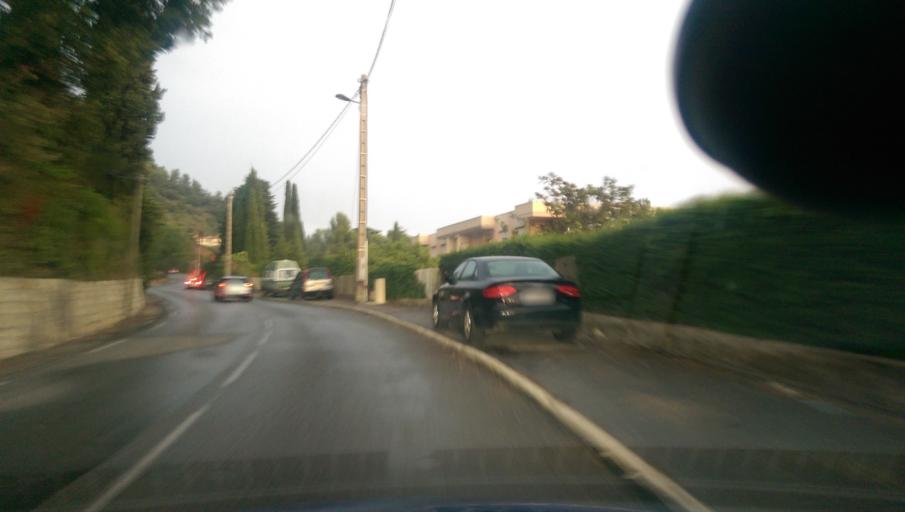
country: FR
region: Provence-Alpes-Cote d'Azur
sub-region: Departement des Alpes-Maritimes
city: Grasse
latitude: 43.6657
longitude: 6.9336
